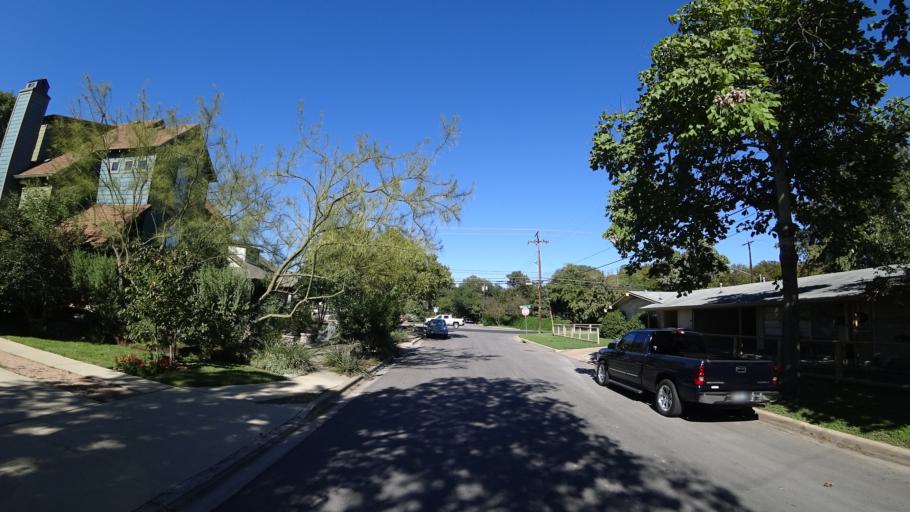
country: US
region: Texas
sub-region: Travis County
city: Austin
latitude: 30.3266
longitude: -97.7481
